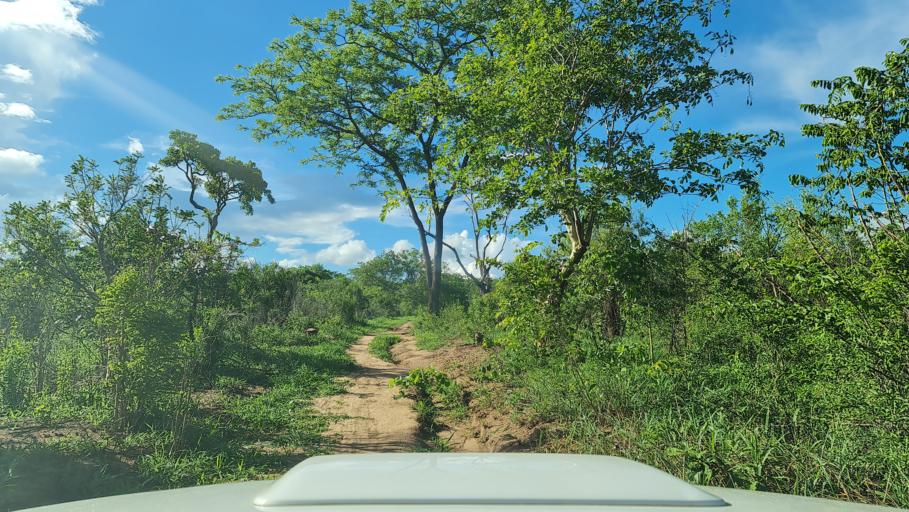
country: MZ
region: Nampula
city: Ilha de Mocambique
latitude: -15.2540
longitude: 40.1823
